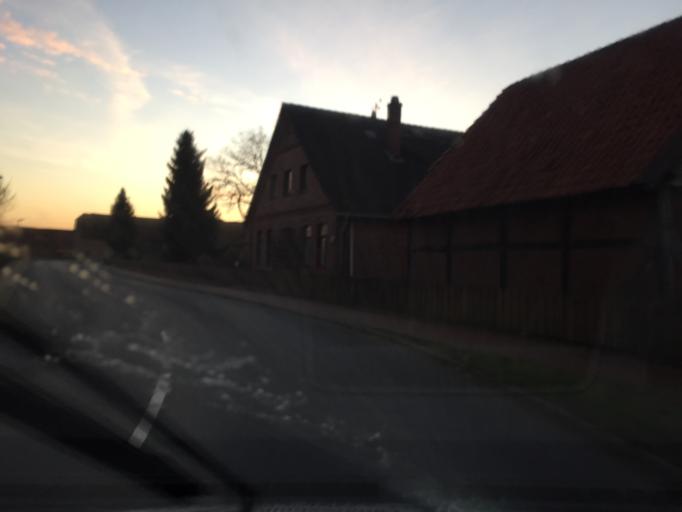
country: DE
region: Lower Saxony
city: Steyerberg
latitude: 52.5929
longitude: 8.9763
